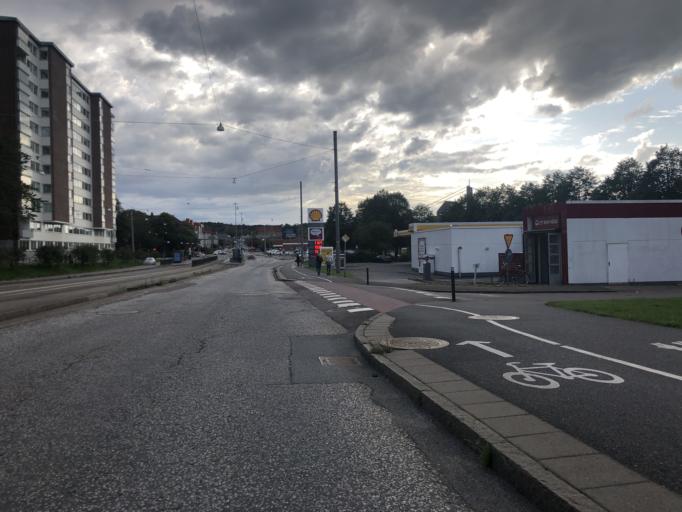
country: SE
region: Vaestra Goetaland
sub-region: Goteborg
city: Majorna
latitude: 57.6930
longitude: 11.9175
